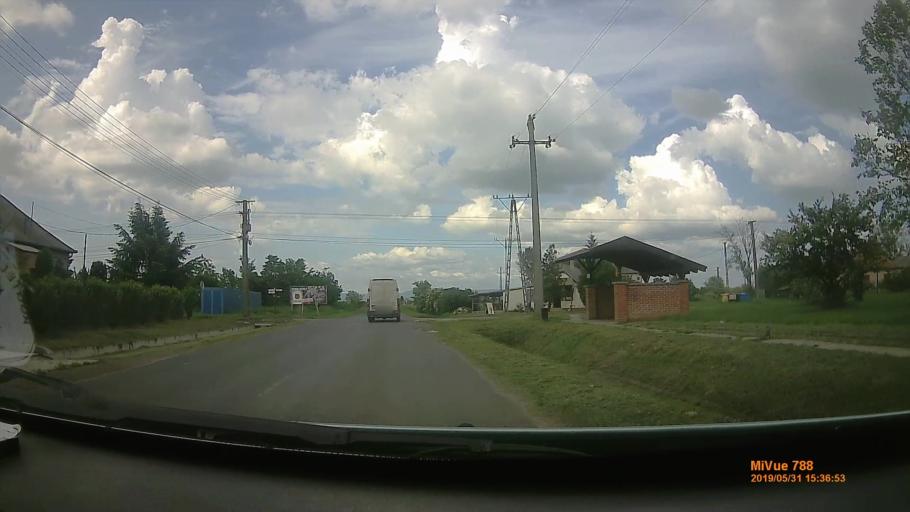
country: HU
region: Borsod-Abauj-Zemplen
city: Prugy
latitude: 48.0874
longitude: 21.2407
